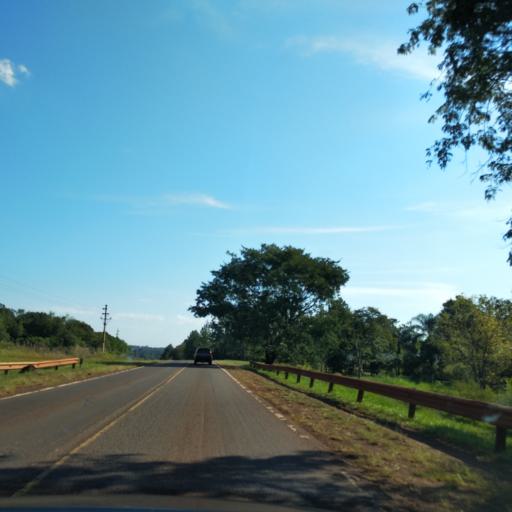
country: AR
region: Misiones
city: Gobernador Roca
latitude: -27.1684
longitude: -55.4440
